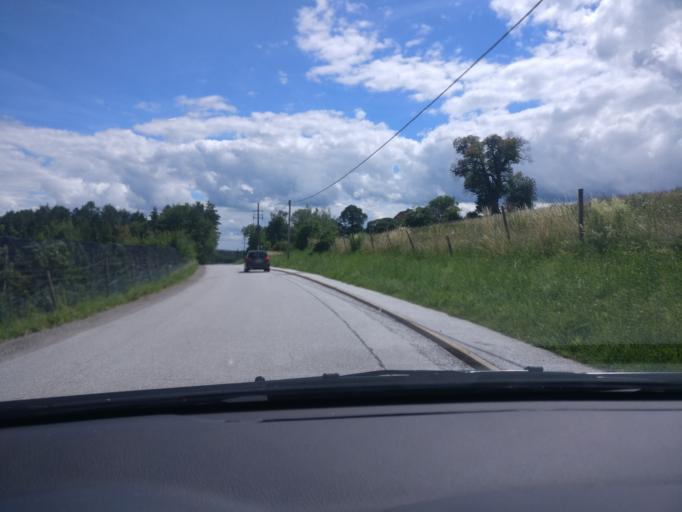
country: AT
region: Styria
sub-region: Politischer Bezirk Weiz
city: Nitscha
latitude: 47.1234
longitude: 15.7339
